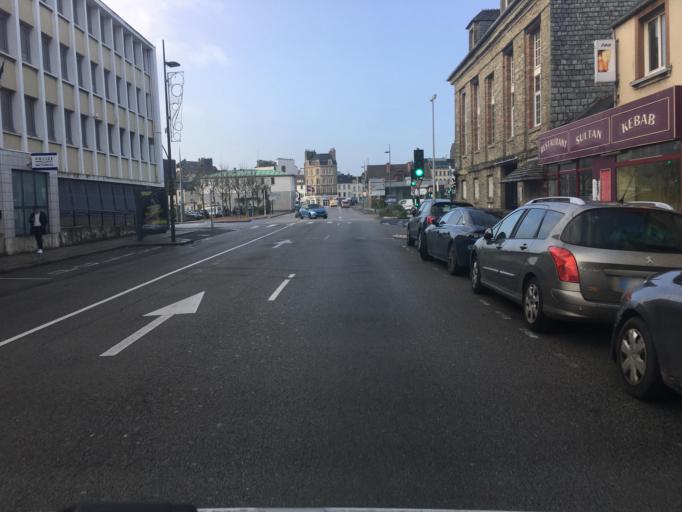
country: FR
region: Lower Normandy
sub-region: Departement de la Manche
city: Cherbourg-Octeville
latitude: 49.6391
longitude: -1.6184
